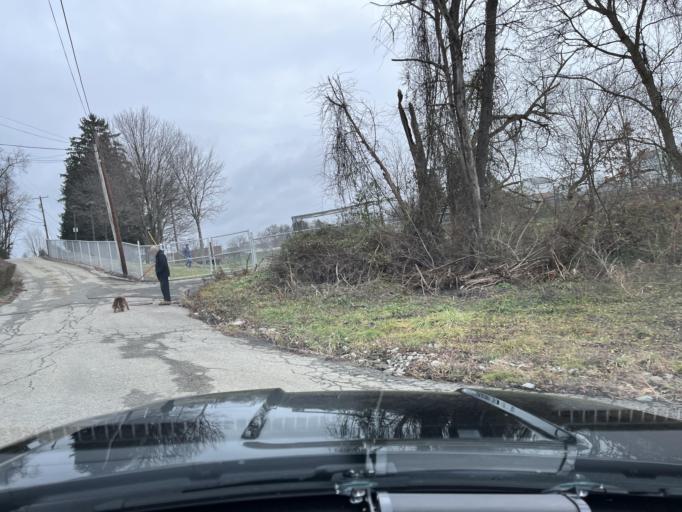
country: US
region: Pennsylvania
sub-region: Fayette County
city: South Uniontown
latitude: 39.8922
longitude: -79.7512
